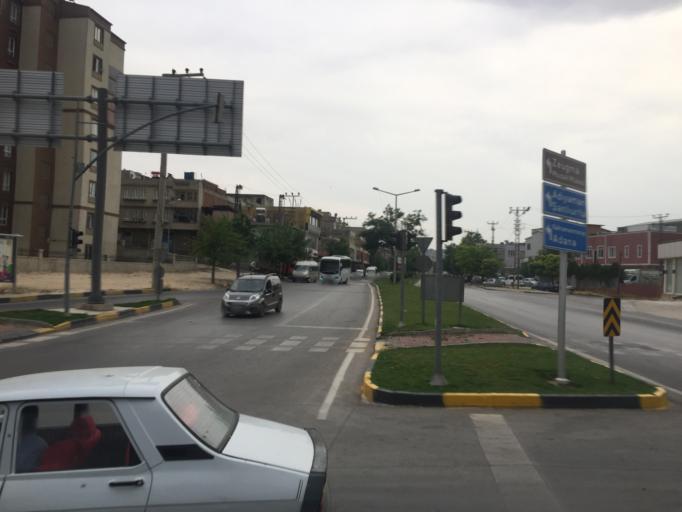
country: TR
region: Gaziantep
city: Gaziantep
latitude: 37.0550
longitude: 37.4154
